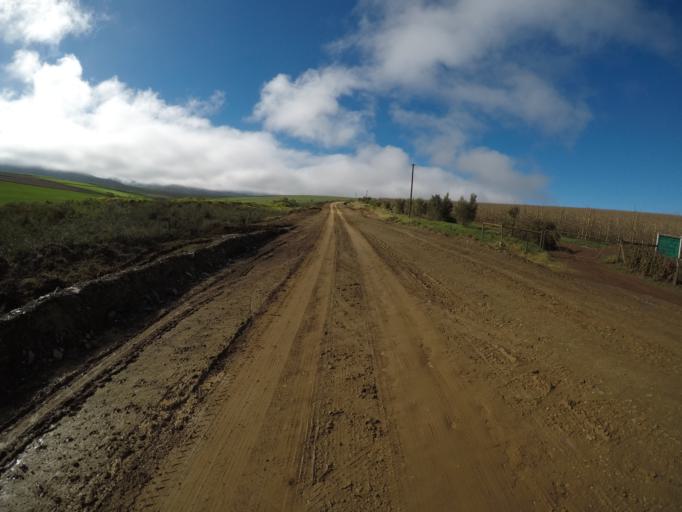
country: ZA
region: Western Cape
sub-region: Overberg District Municipality
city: Caledon
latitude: -34.1098
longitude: 19.7536
